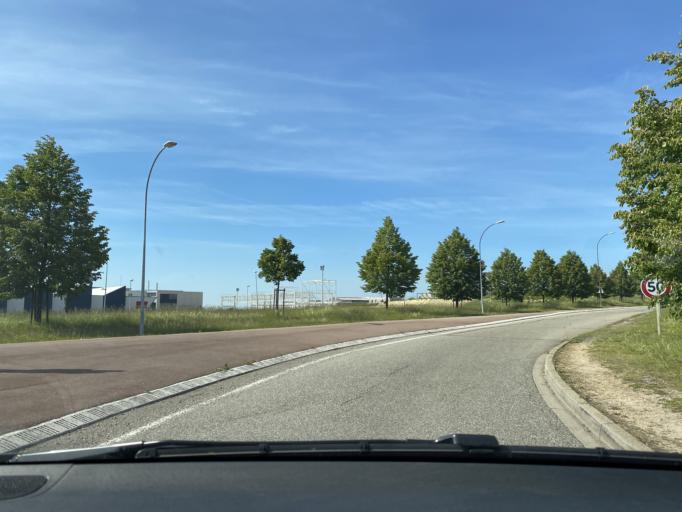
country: FR
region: Lorraine
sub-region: Departement de la Moselle
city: OEting
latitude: 49.1644
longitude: 6.9186
